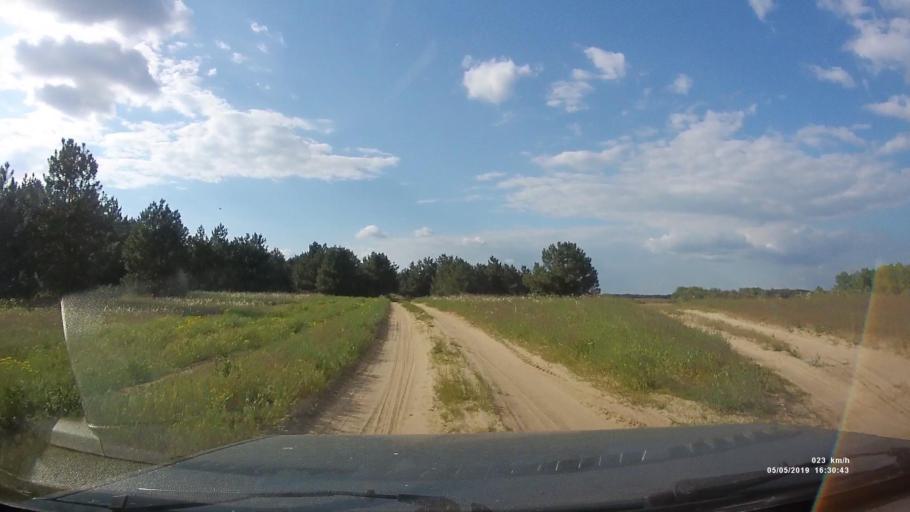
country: RU
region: Rostov
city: Ust'-Donetskiy
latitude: 47.7744
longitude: 41.0159
